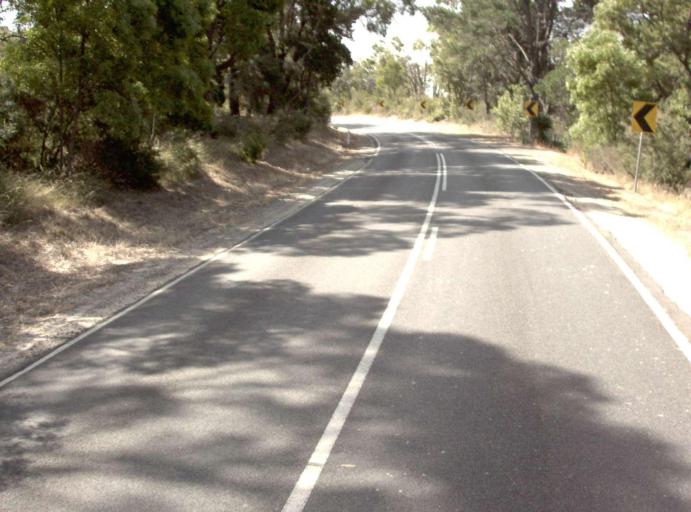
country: AU
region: Victoria
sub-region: Wellington
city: Sale
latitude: -38.2644
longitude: 147.1470
